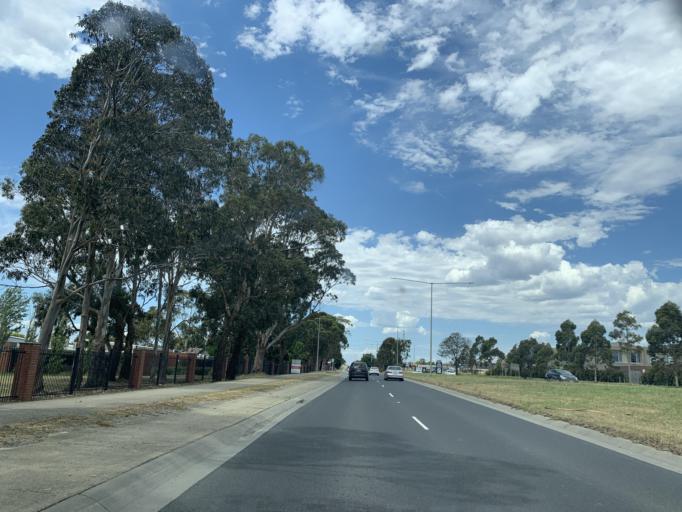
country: AU
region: Victoria
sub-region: Casey
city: Cranbourne West
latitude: -38.1096
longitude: 145.2556
